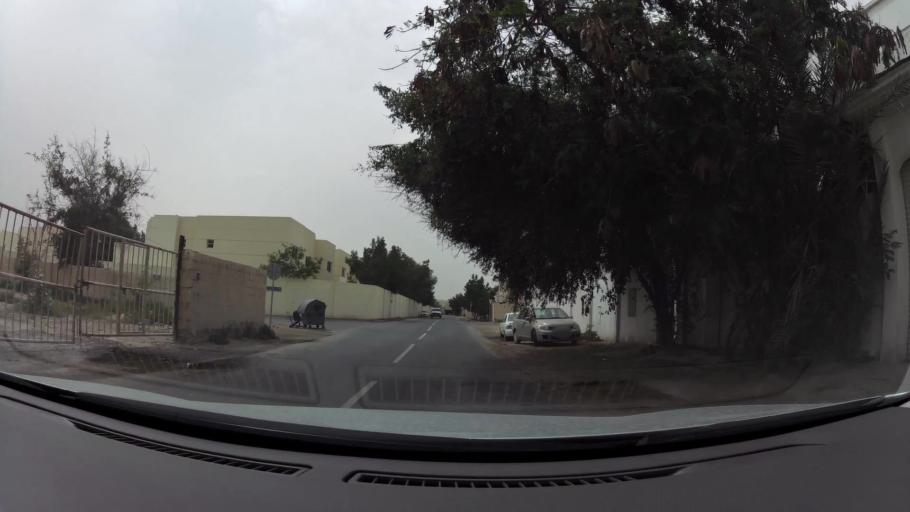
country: QA
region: Baladiyat ad Dawhah
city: Doha
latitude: 25.2477
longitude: 51.5649
